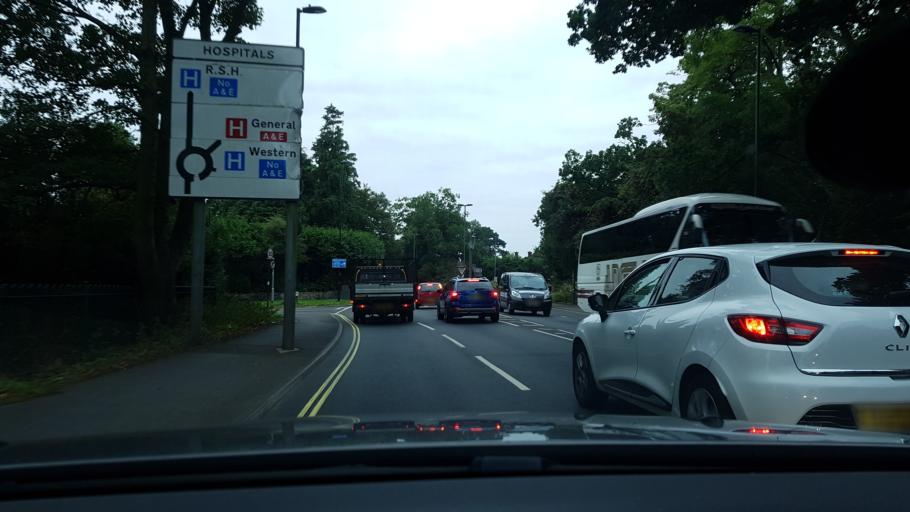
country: GB
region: England
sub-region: Southampton
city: Southampton
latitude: 50.9416
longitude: -1.4065
